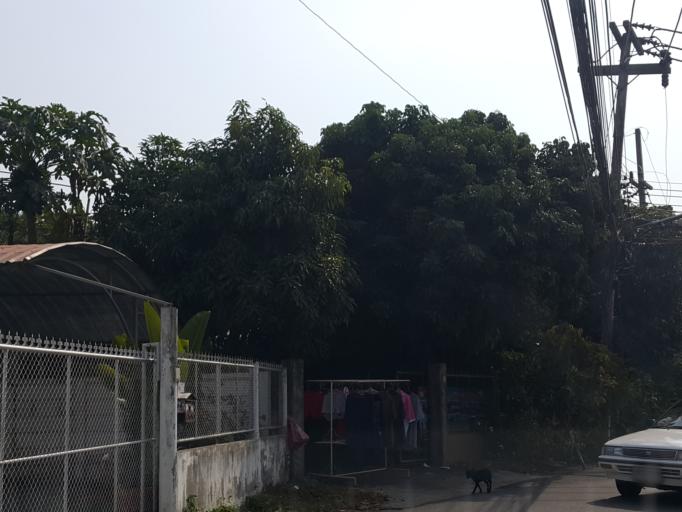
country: TH
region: Chiang Mai
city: San Kamphaeng
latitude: 18.8110
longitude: 99.1220
